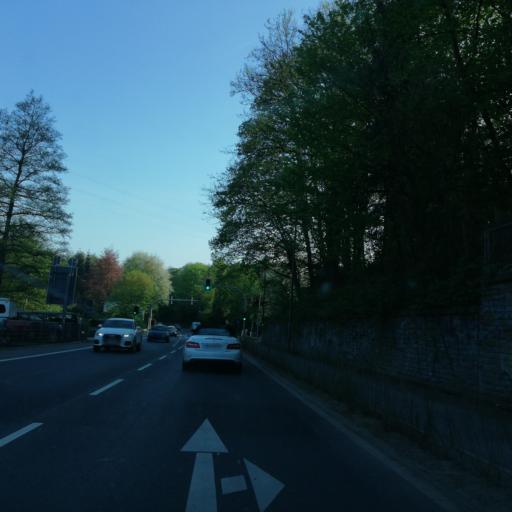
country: DE
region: North Rhine-Westphalia
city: Herdecke
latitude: 51.4134
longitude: 7.4315
